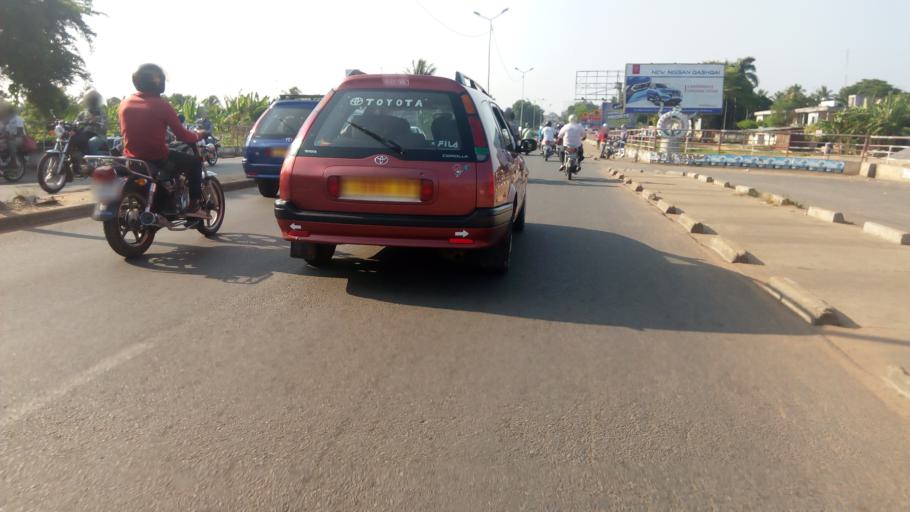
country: TG
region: Maritime
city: Lome
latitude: 6.1599
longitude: 1.2019
